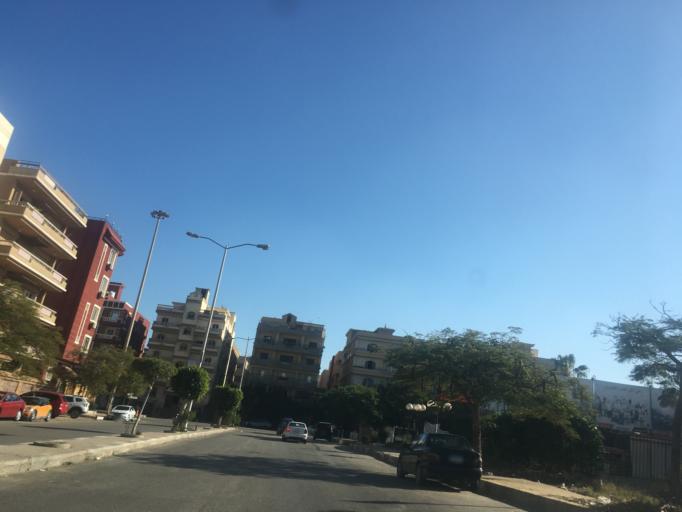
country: EG
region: Al Jizah
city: Madinat Sittah Uktubar
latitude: 29.9814
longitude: 30.9459
